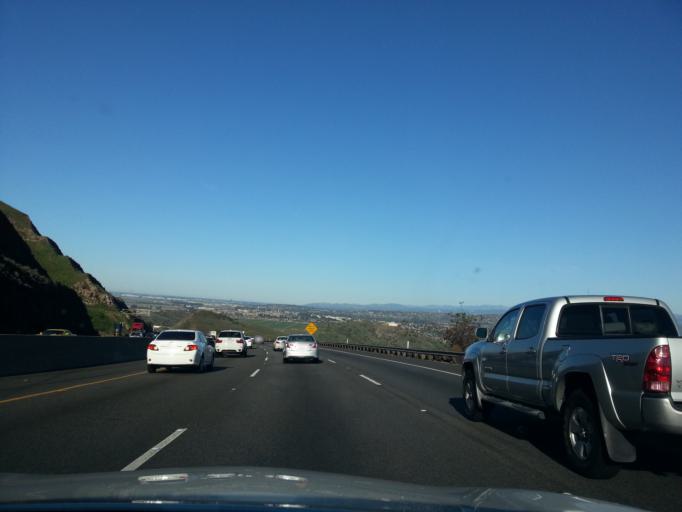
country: US
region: California
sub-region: Ventura County
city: Casa Conejo
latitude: 34.2009
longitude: -118.9645
